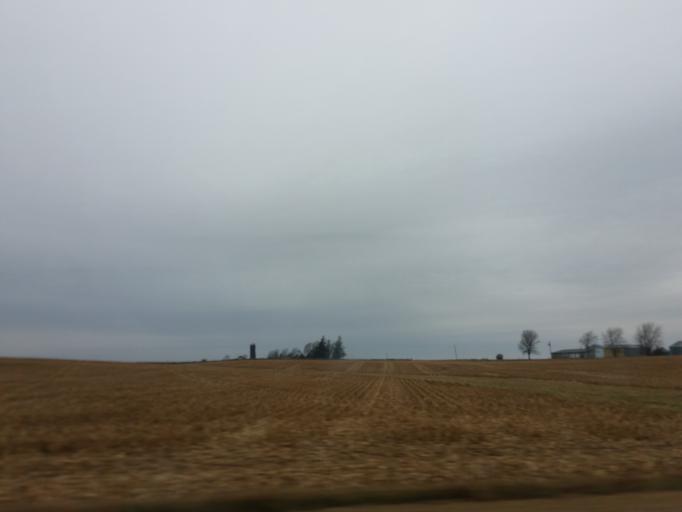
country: US
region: Iowa
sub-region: Black Hawk County
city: La Porte City
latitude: 42.2091
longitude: -92.2018
